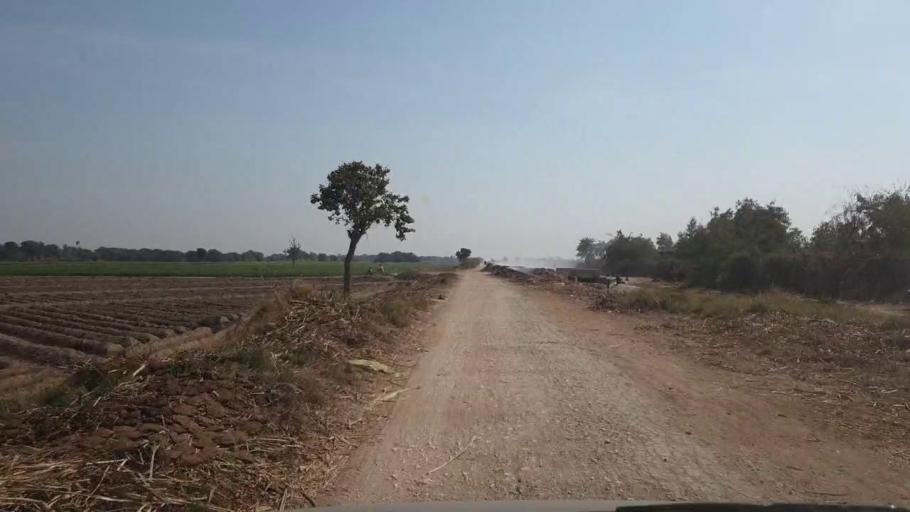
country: PK
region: Sindh
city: Chambar
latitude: 25.3659
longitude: 68.7938
